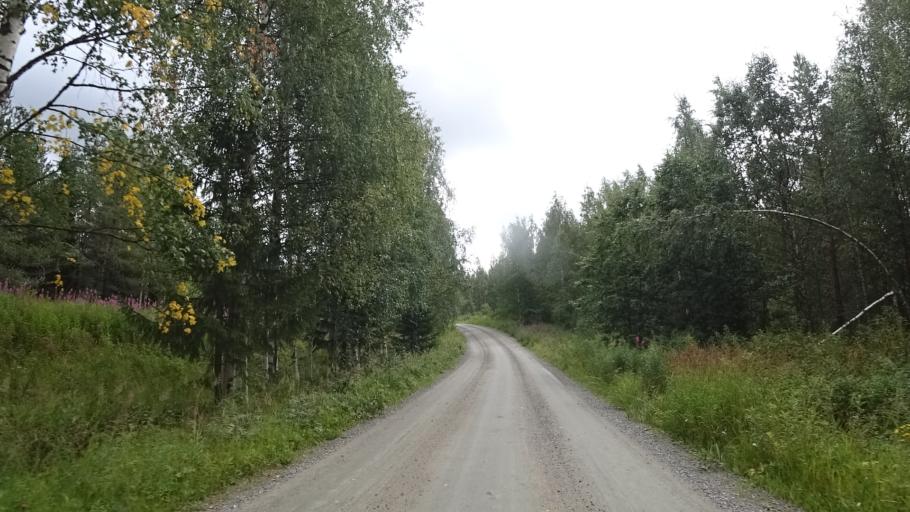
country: FI
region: North Karelia
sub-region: Joensuu
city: Ilomantsi
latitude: 62.9326
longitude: 31.3074
